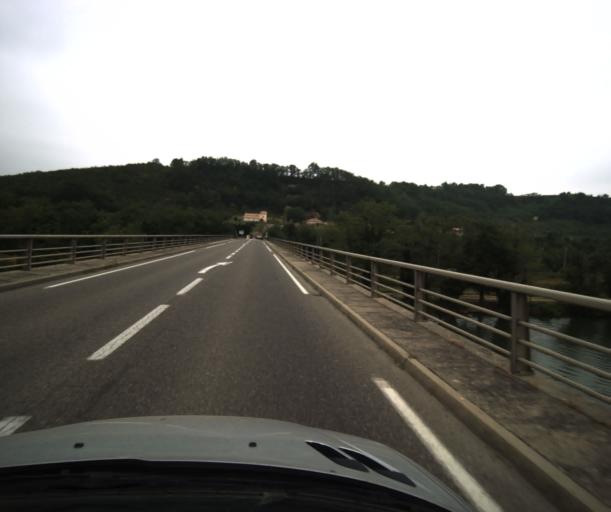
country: FR
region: Midi-Pyrenees
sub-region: Departement du Tarn-et-Garonne
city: Saint-Nicolas-de-la-Grave
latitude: 44.0847
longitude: 0.9865
